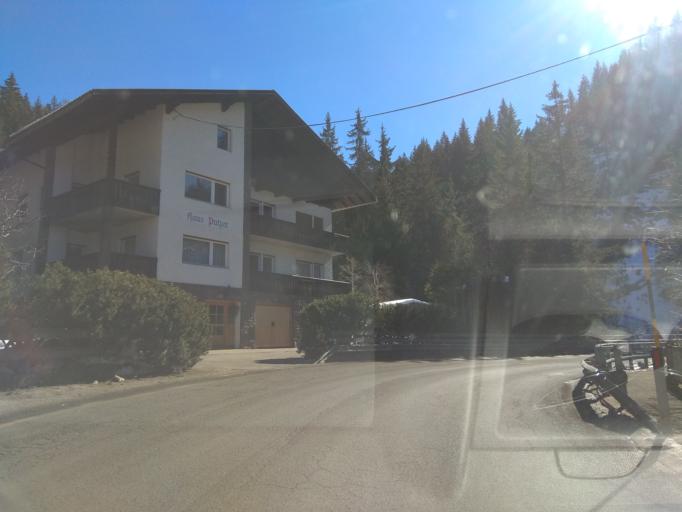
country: IT
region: Trentino-Alto Adige
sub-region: Bolzano
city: Nova Levante
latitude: 46.4166
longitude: 11.5693
